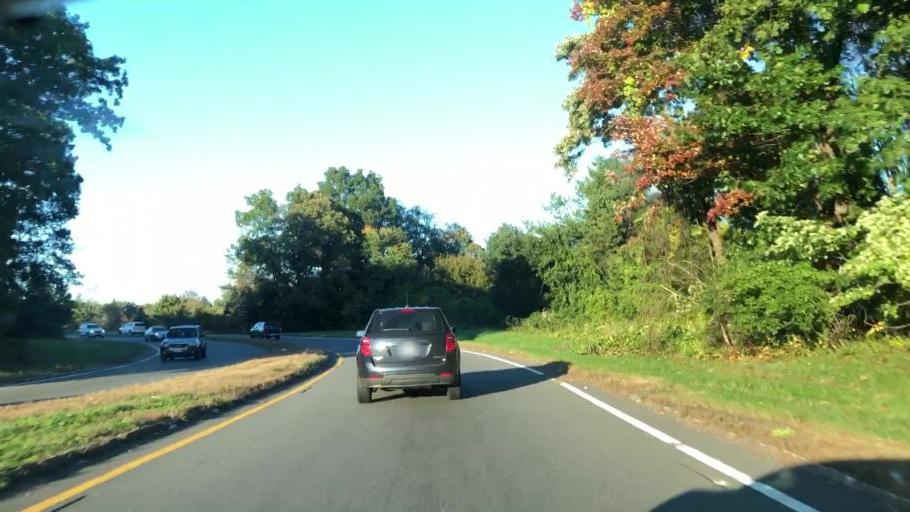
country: US
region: Massachusetts
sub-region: Essex County
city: Lawrence
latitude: 42.6627
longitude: -71.1917
